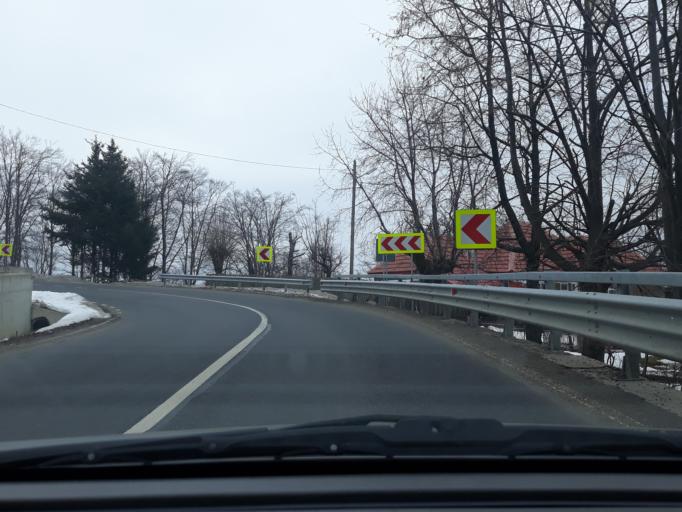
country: RO
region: Bihor
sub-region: Comuna Sinteu
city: Sinteu
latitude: 47.1215
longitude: 22.4622
